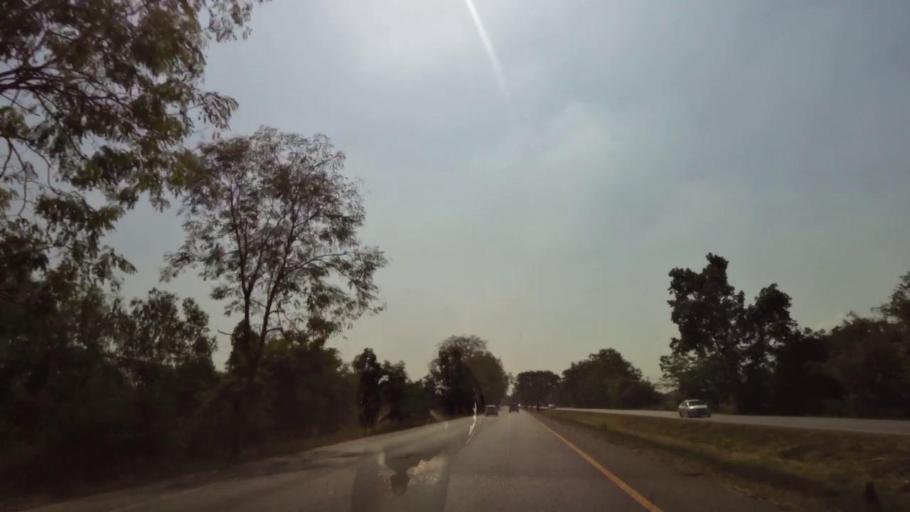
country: TH
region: Phichit
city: Wachira Barami
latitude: 16.3685
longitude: 100.1320
